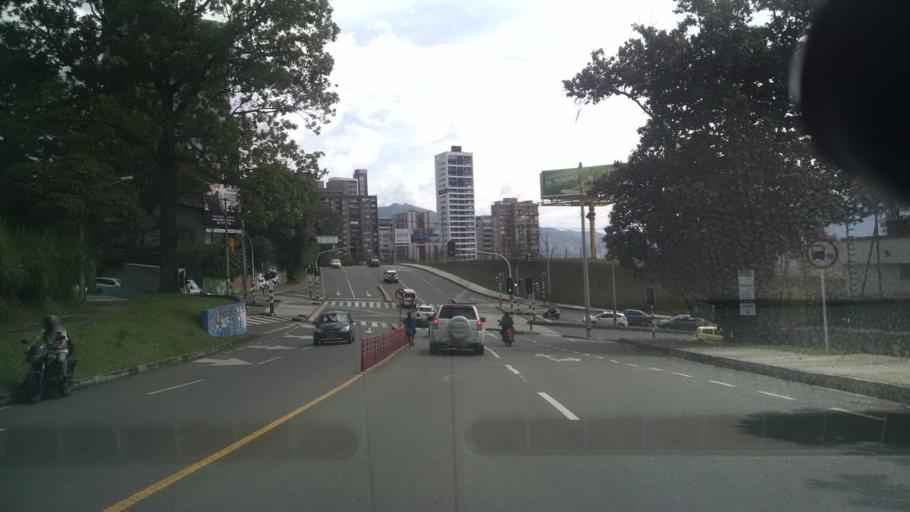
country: CO
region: Antioquia
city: Envigado
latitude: 6.1942
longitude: -75.5715
